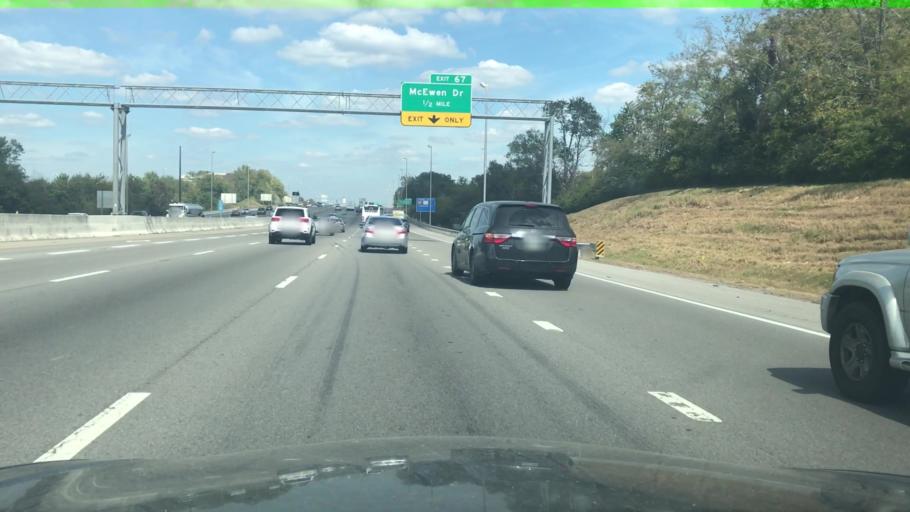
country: US
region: Tennessee
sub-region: Williamson County
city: Franklin
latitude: 35.9240
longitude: -86.8222
